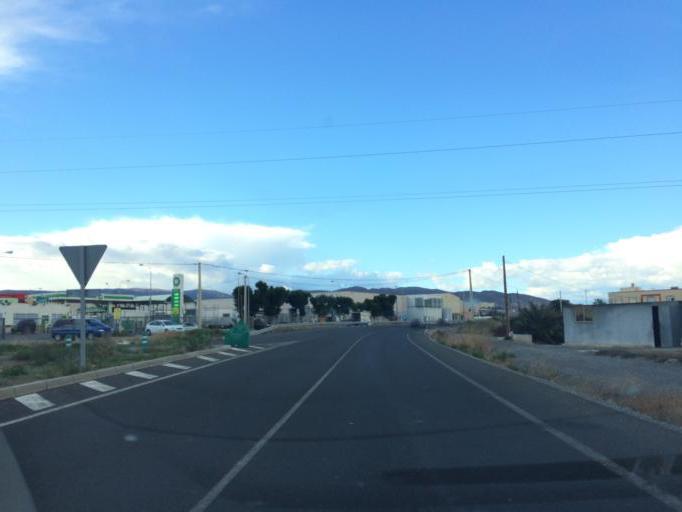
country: ES
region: Andalusia
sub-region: Provincia de Almeria
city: Almeria
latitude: 36.8406
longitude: -2.4188
